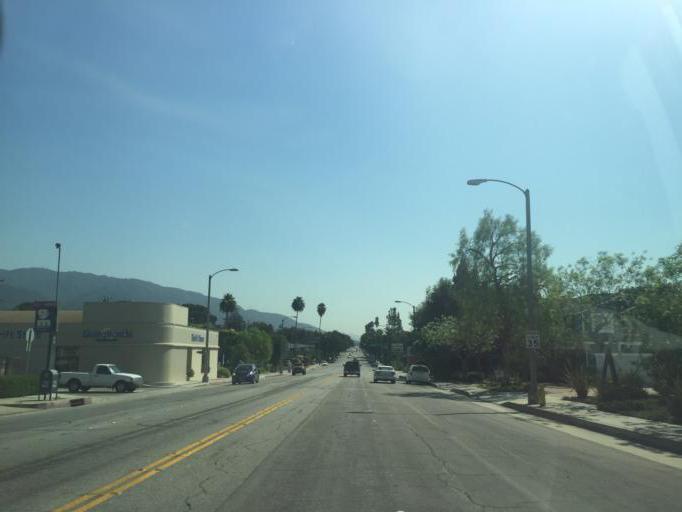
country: US
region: California
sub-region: Los Angeles County
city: Arcadia
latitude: 34.1511
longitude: -118.0202
